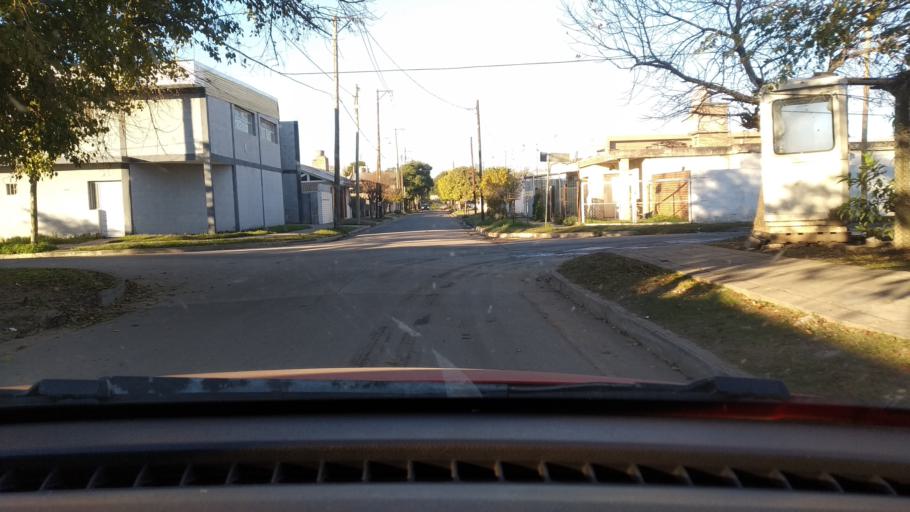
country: AR
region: Cordoba
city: Villa Allende
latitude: -31.3442
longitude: -64.2294
